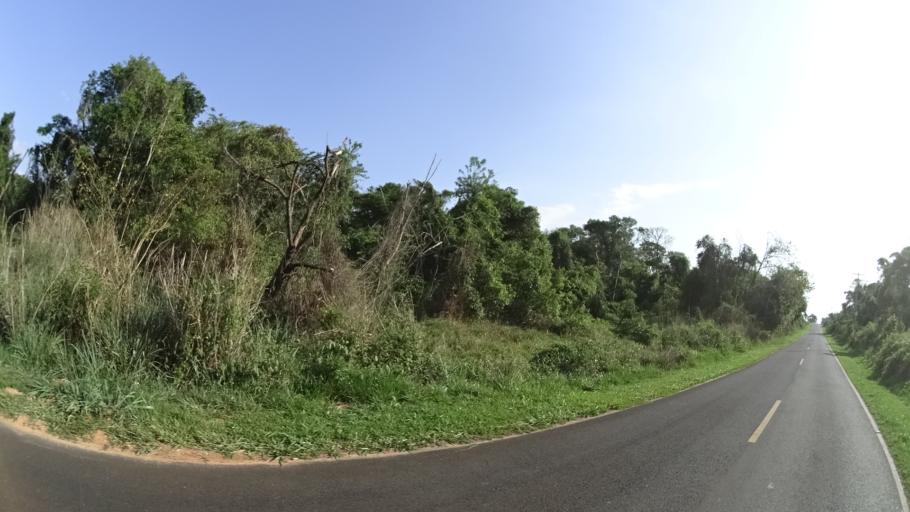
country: BR
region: Sao Paulo
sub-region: Urupes
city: Urupes
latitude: -21.3798
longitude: -49.4862
